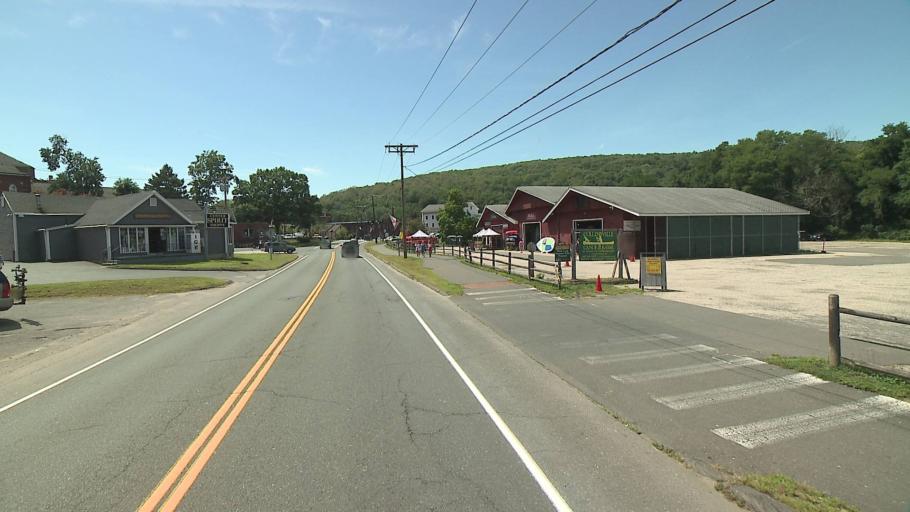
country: US
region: Connecticut
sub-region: Hartford County
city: Collinsville
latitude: 41.8120
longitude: -72.9225
